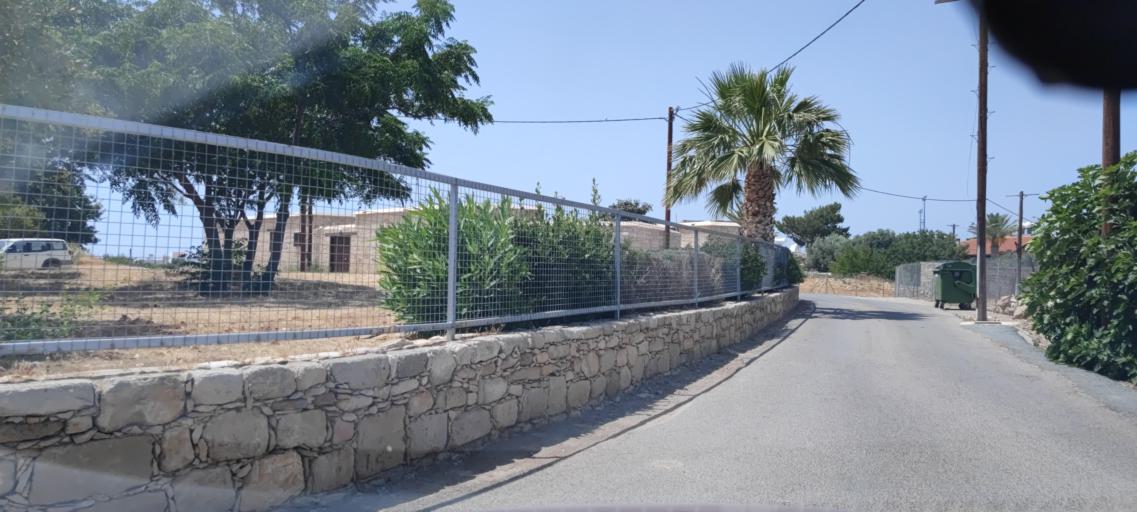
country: CY
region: Limassol
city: Pissouri
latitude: 34.7085
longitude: 32.5742
